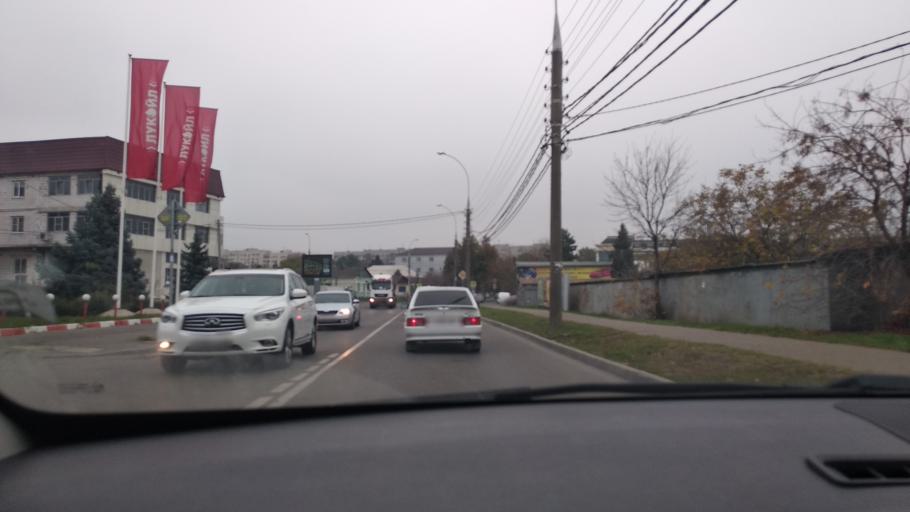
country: RU
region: Krasnodarskiy
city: Krasnodar
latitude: 45.0239
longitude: 39.0089
